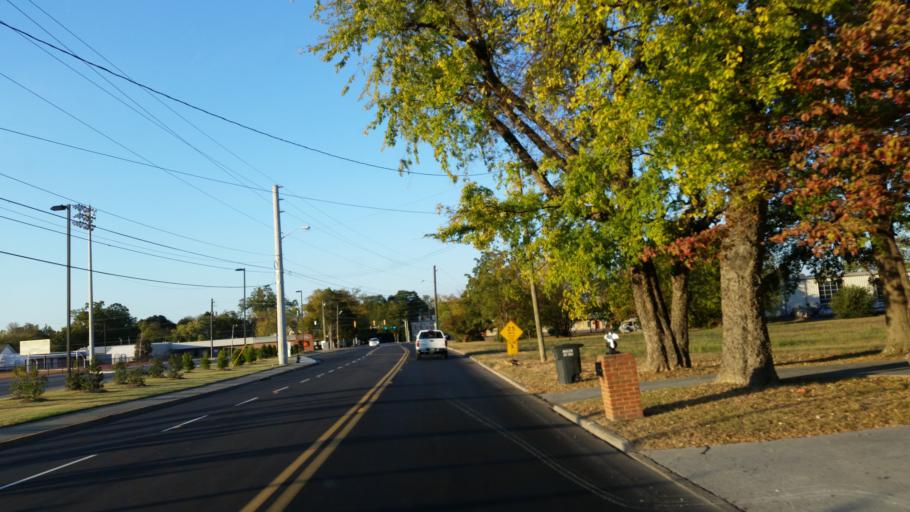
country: US
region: Georgia
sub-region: Gordon County
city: Calhoun
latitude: 34.5002
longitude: -84.9549
